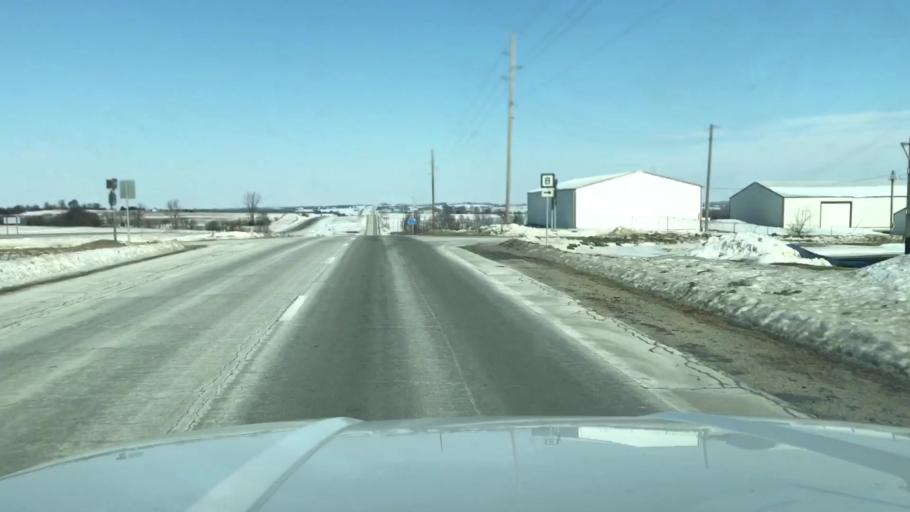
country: US
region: Missouri
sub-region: Andrew County
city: Savannah
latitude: 40.1137
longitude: -94.8697
